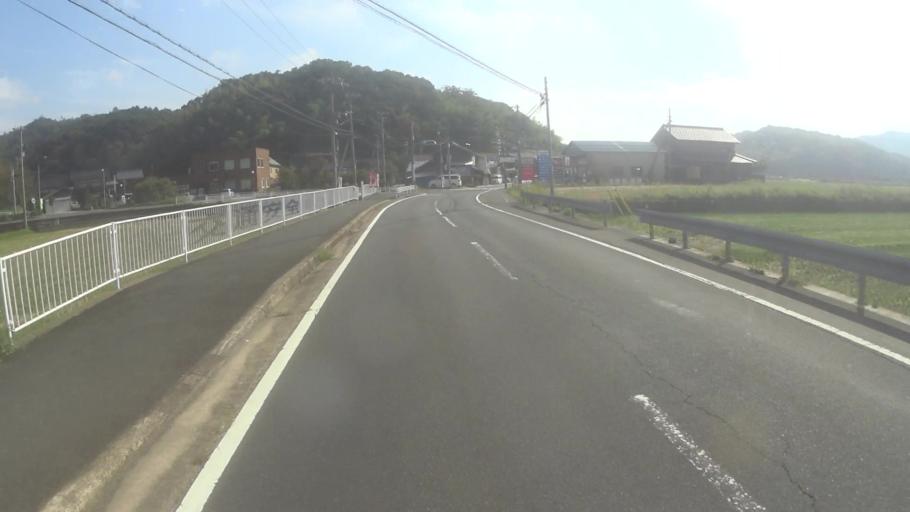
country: JP
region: Kyoto
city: Miyazu
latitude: 35.7121
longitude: 135.1064
